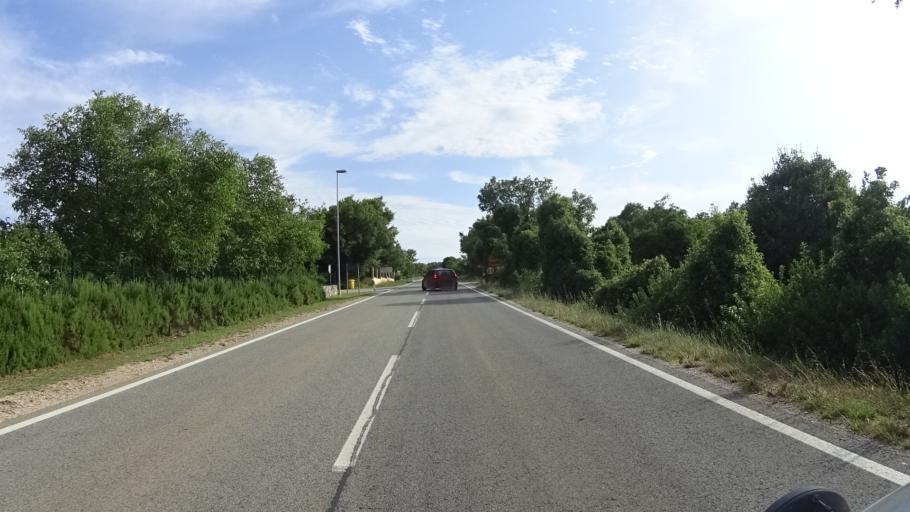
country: HR
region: Istarska
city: Rasa
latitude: 45.0681
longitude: 14.0919
